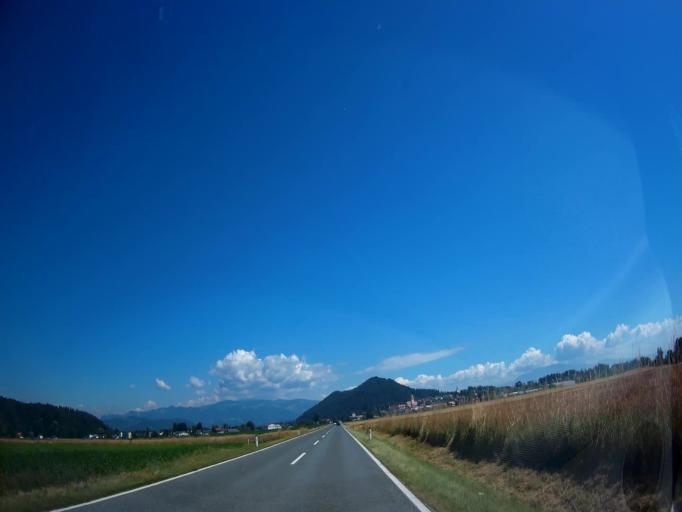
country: AT
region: Carinthia
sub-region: Politischer Bezirk Volkermarkt
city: Eberndorf
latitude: 46.5804
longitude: 14.6321
